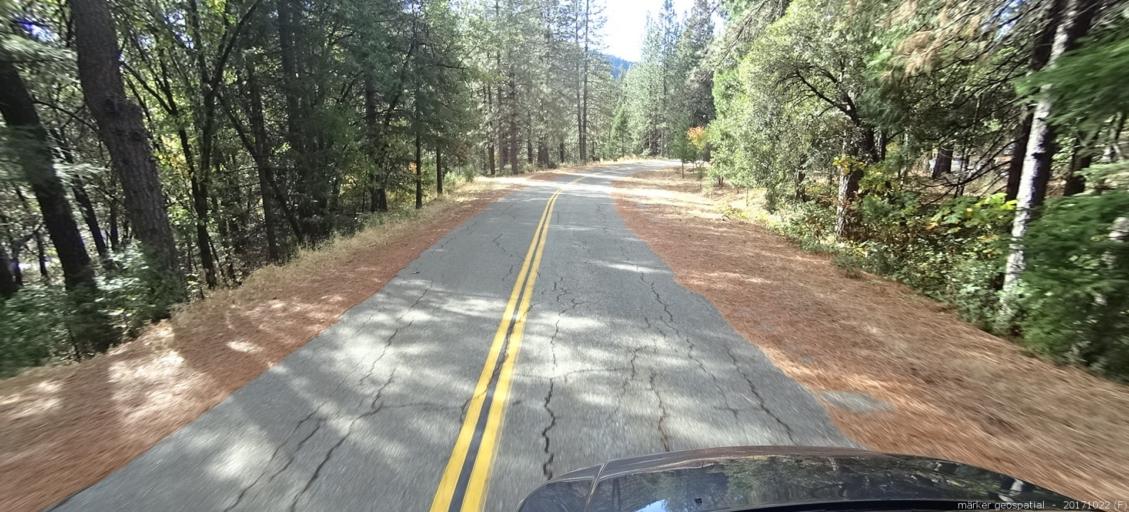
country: US
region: California
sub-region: Siskiyou County
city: Dunsmuir
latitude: 41.0676
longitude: -122.3620
